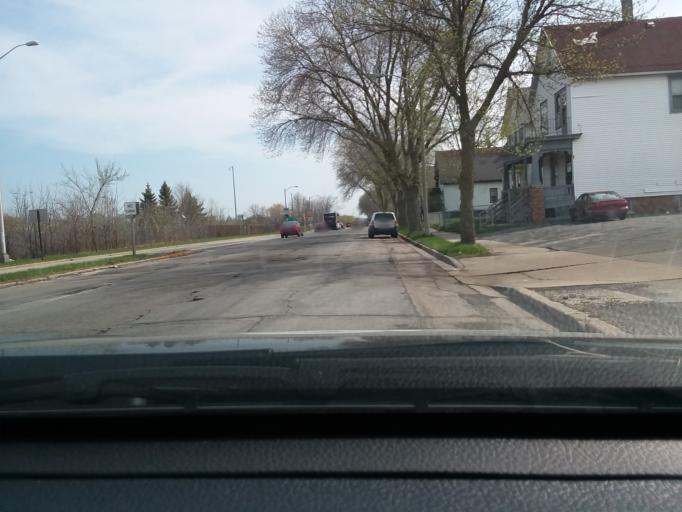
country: US
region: Wisconsin
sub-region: Milwaukee County
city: Milwaukee
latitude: 43.0726
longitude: -87.9215
